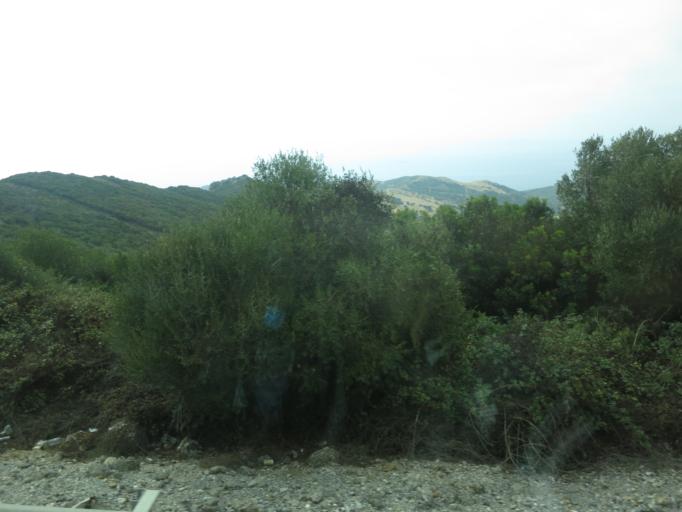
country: ES
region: Andalusia
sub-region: Provincia de Cadiz
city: Tarifa
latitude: 36.0578
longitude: -5.5455
